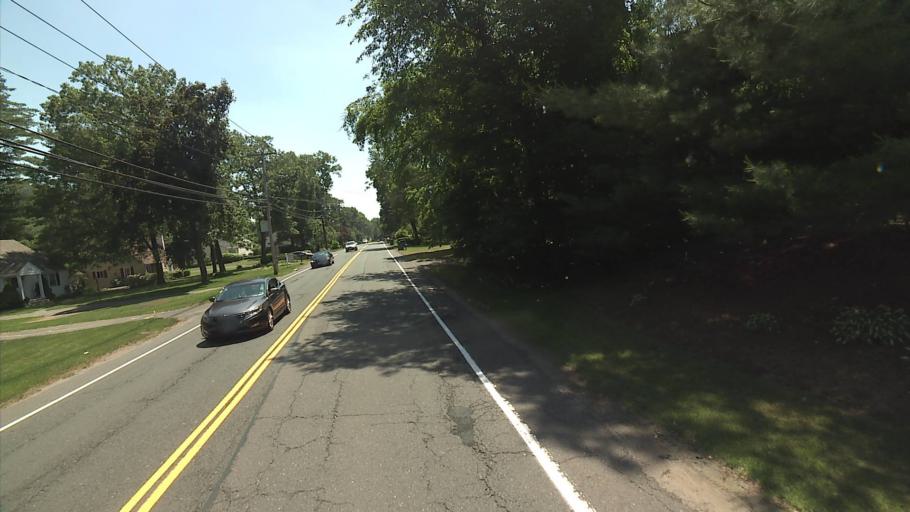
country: US
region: Connecticut
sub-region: Hartford County
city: South Windsor
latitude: 41.8180
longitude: -72.5894
